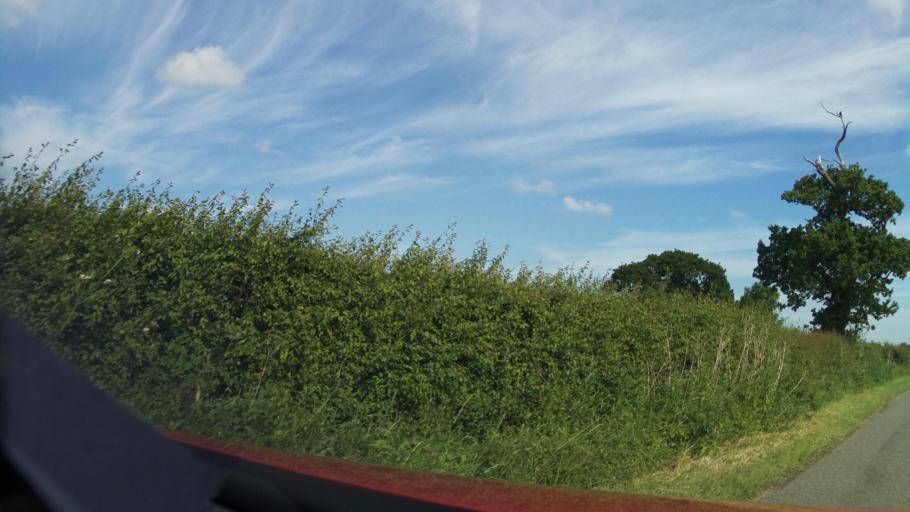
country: GB
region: England
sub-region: Lincolnshire
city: Skellingthorpe
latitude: 53.1432
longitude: -0.6331
